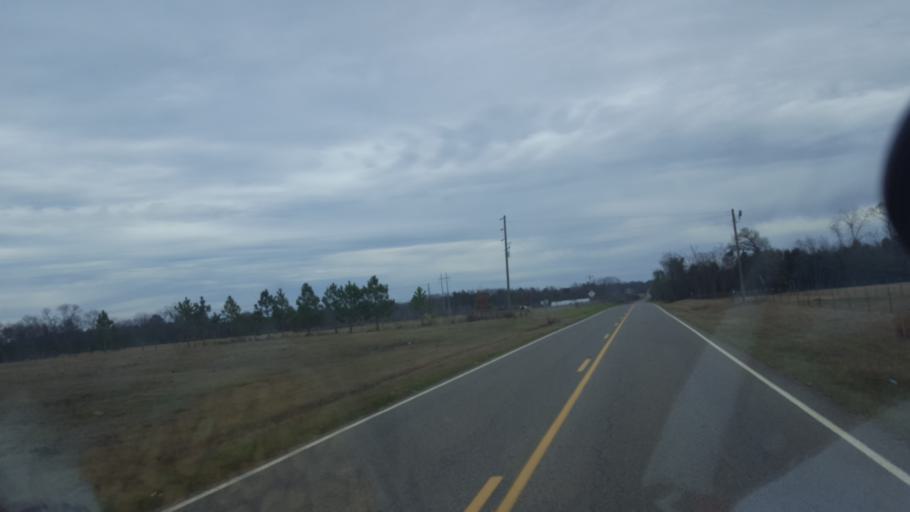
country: US
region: Georgia
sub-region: Ben Hill County
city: Fitzgerald
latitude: 31.7438
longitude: -83.3090
